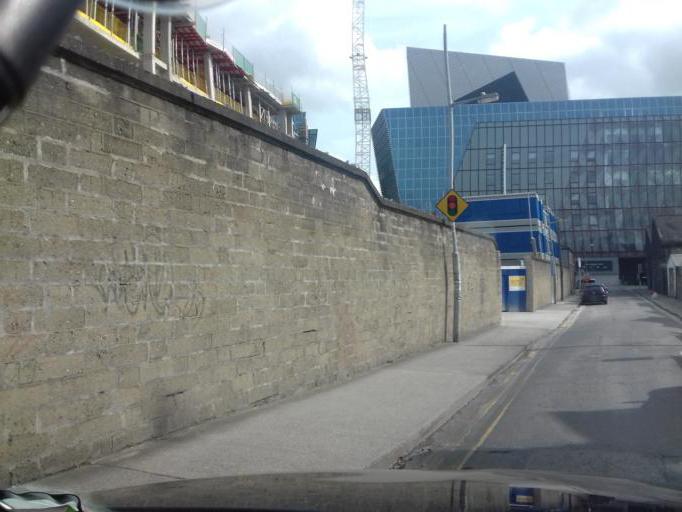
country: IE
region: Leinster
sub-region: Dublin City
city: Dublin
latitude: 53.3446
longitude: -6.2423
